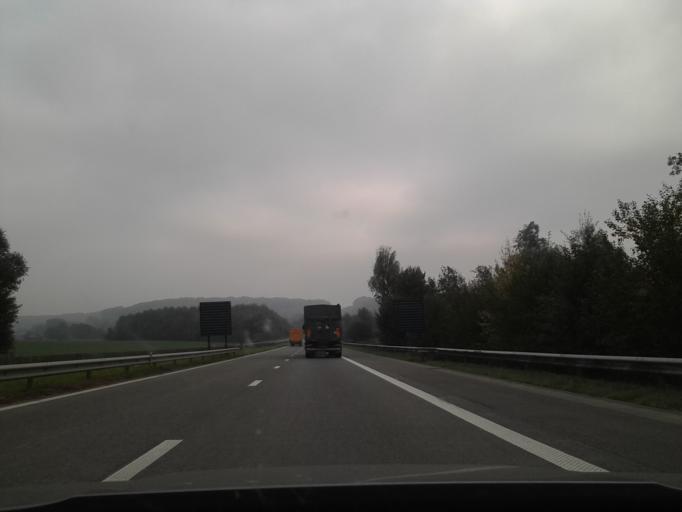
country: BE
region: Wallonia
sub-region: Province du Hainaut
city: Frasnes-lez-Buissenal
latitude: 50.6592
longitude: 3.6438
